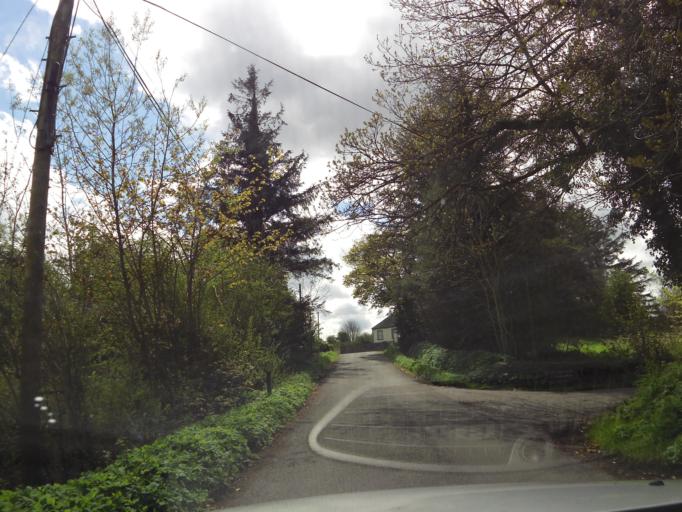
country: IE
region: Connaught
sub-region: Maigh Eo
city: Kiltamagh
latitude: 53.8010
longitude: -8.9703
